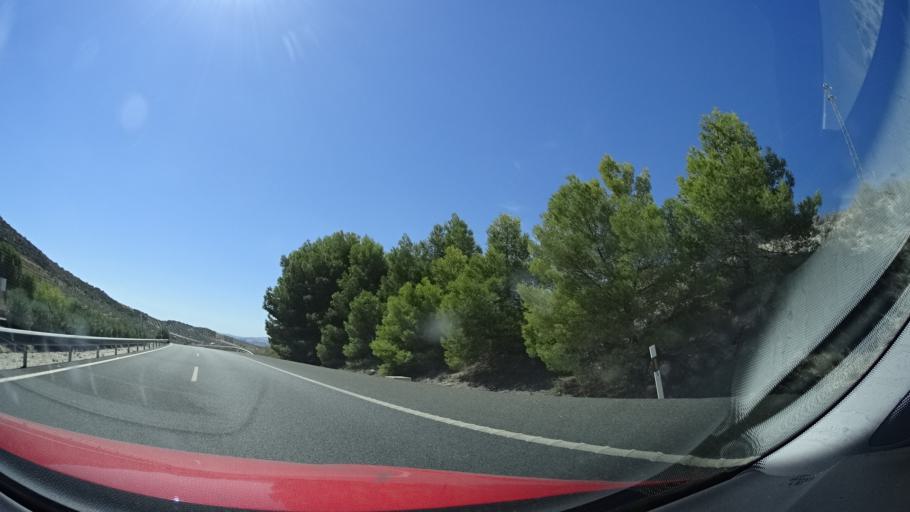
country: ES
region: Andalusia
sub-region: Provincia de Sevilla
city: Estepa
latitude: 37.2924
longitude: -4.9065
